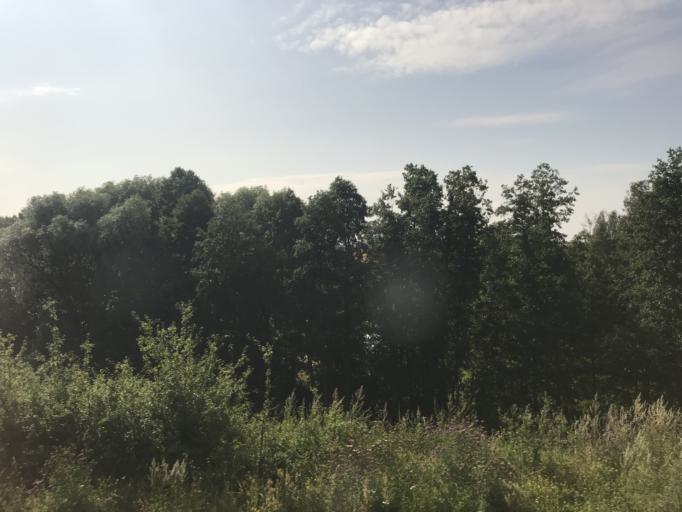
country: PL
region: Kujawsko-Pomorskie
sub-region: Powiat swiecki
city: Bukowiec
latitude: 53.3767
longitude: 18.2876
